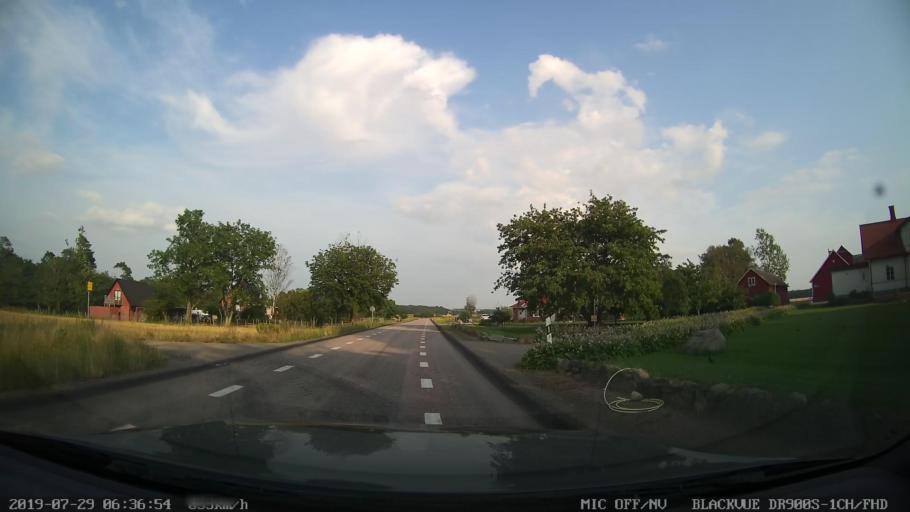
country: SE
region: Skane
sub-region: Helsingborg
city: Odakra
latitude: 56.1074
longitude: 12.7153
